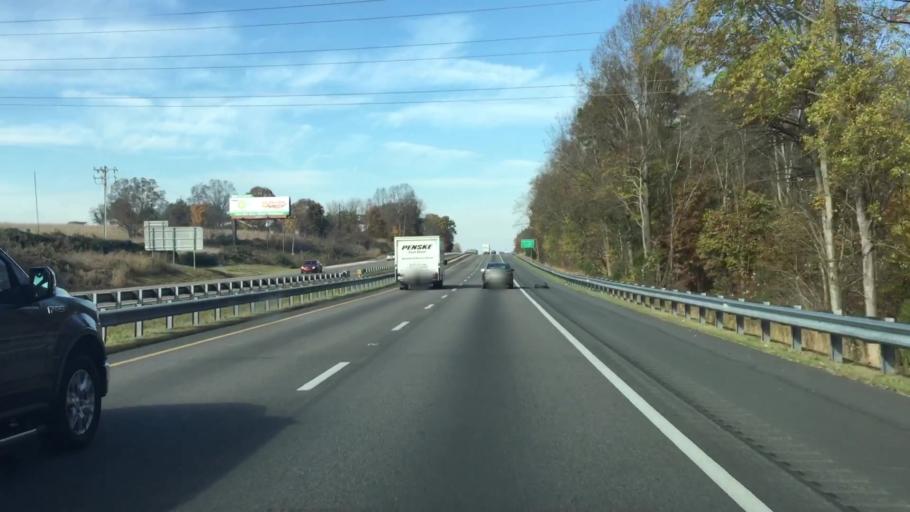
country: US
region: North Carolina
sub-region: Iredell County
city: Statesville
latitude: 35.7572
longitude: -80.8613
